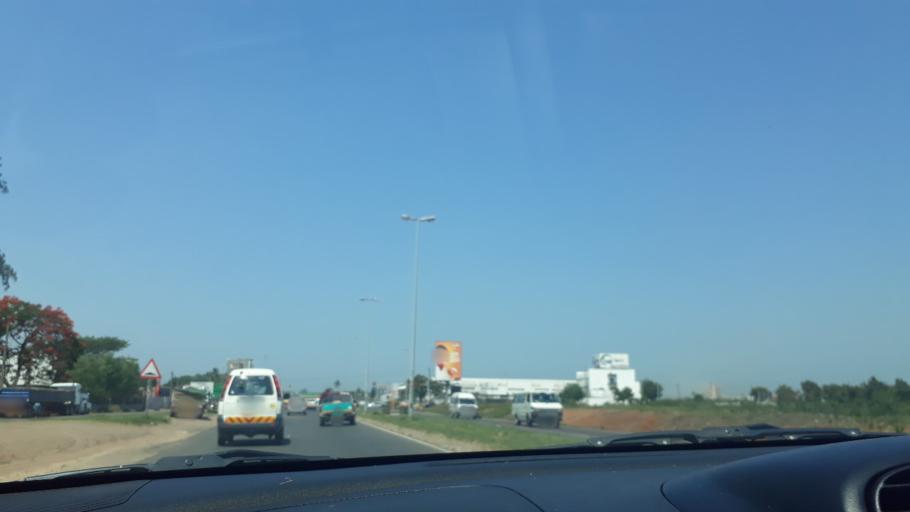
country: MZ
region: Maputo
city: Matola
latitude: -25.9545
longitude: 32.4584
